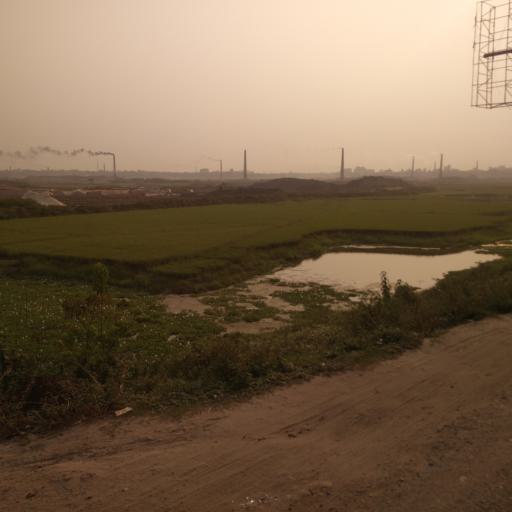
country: BD
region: Dhaka
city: Tungi
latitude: 23.8947
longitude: 90.3472
